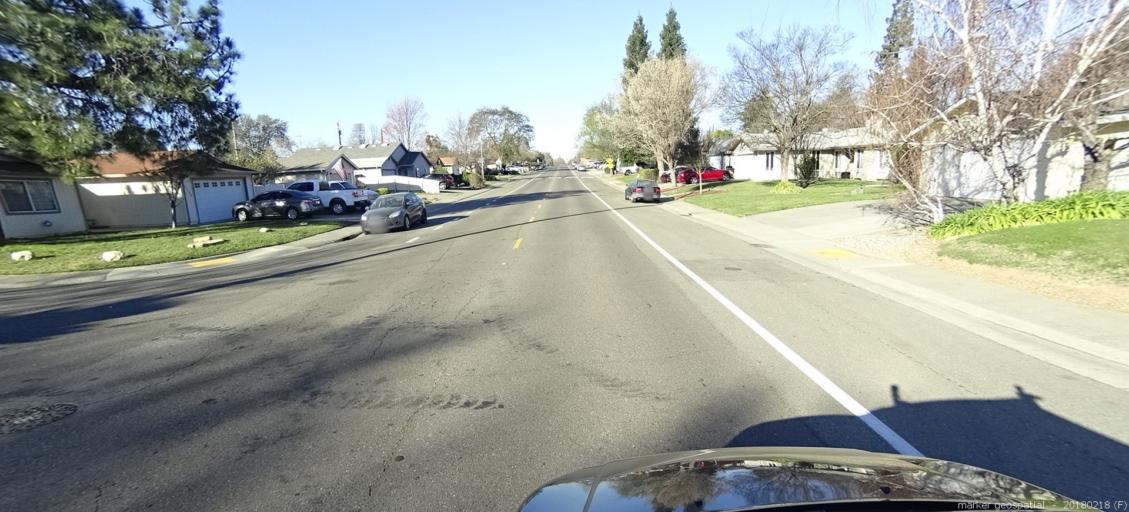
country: US
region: California
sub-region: Sacramento County
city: Orangevale
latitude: 38.6705
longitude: -121.2134
